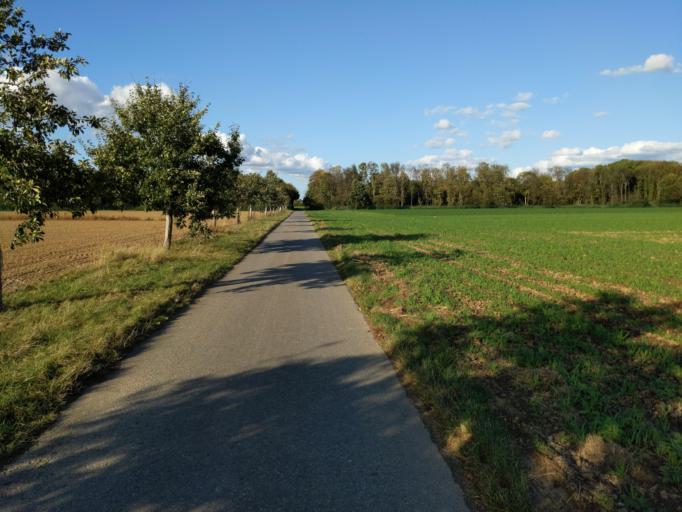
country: DE
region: North Rhine-Westphalia
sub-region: Regierungsbezirk Dusseldorf
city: Kaarst
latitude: 51.2085
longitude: 6.6016
